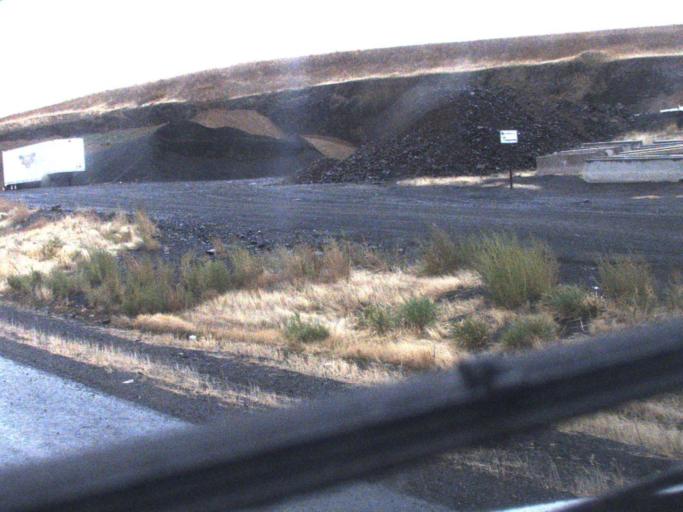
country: US
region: Washington
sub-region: Whitman County
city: Colfax
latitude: 46.9592
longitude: -117.3317
